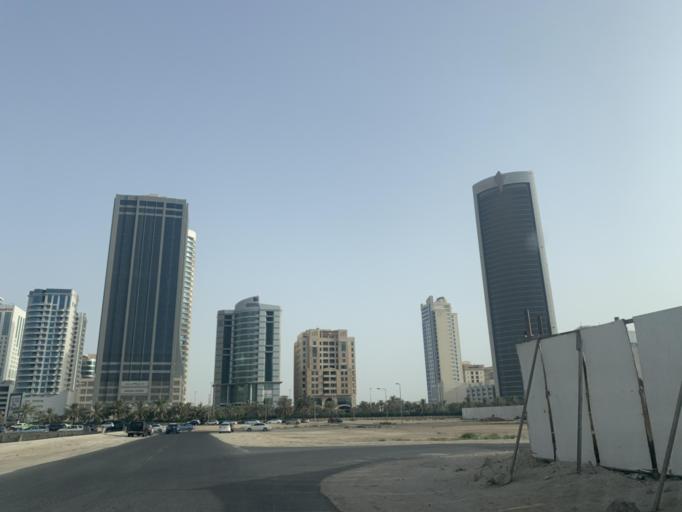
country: BH
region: Manama
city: Jidd Hafs
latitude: 26.2337
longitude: 50.5497
